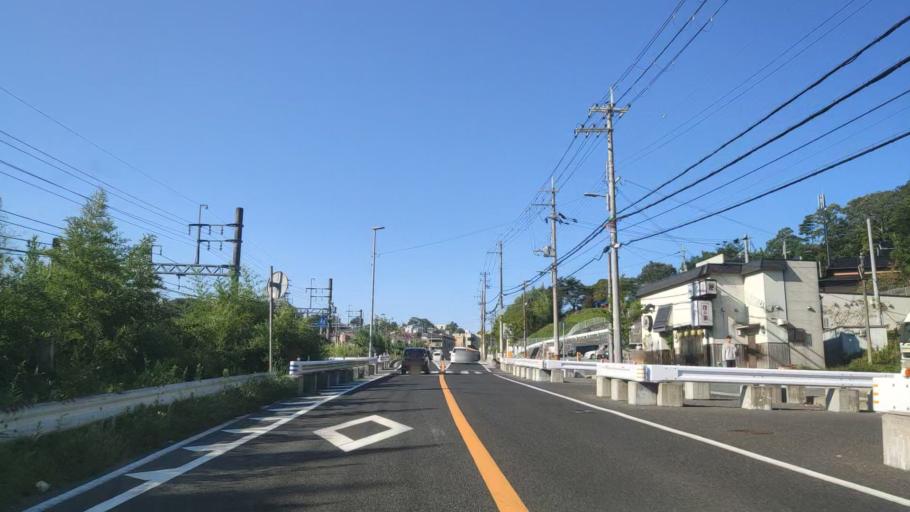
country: JP
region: Hyogo
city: Kobe
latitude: 34.7845
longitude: 135.2046
